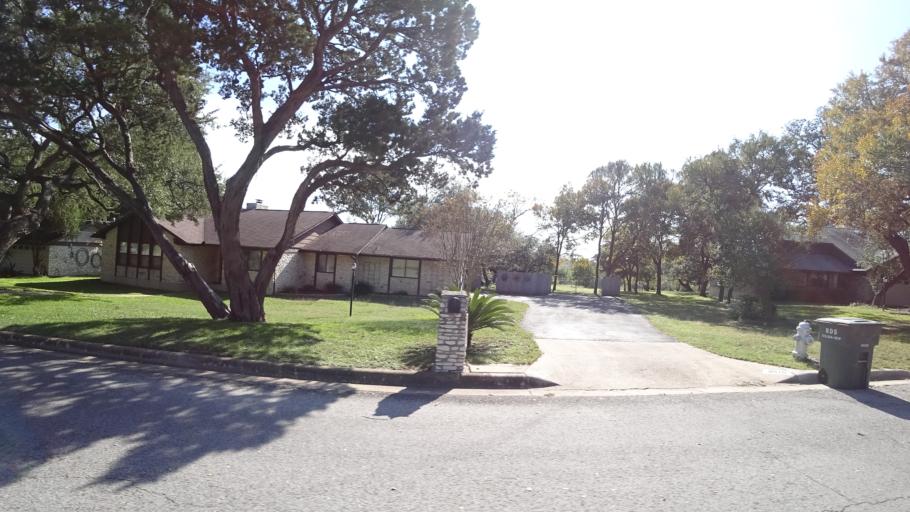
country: US
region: Texas
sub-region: Travis County
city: Shady Hollow
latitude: 30.2174
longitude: -97.9082
